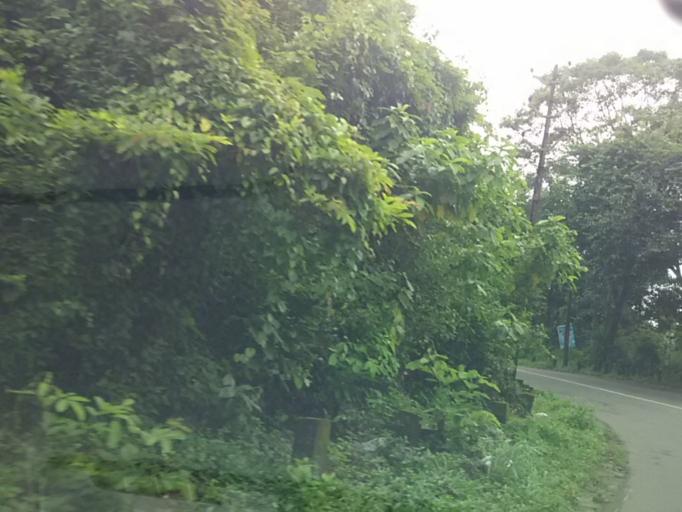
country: IN
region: Kerala
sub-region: Kozhikode
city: Kunnamangalam
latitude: 11.3126
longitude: 75.9217
